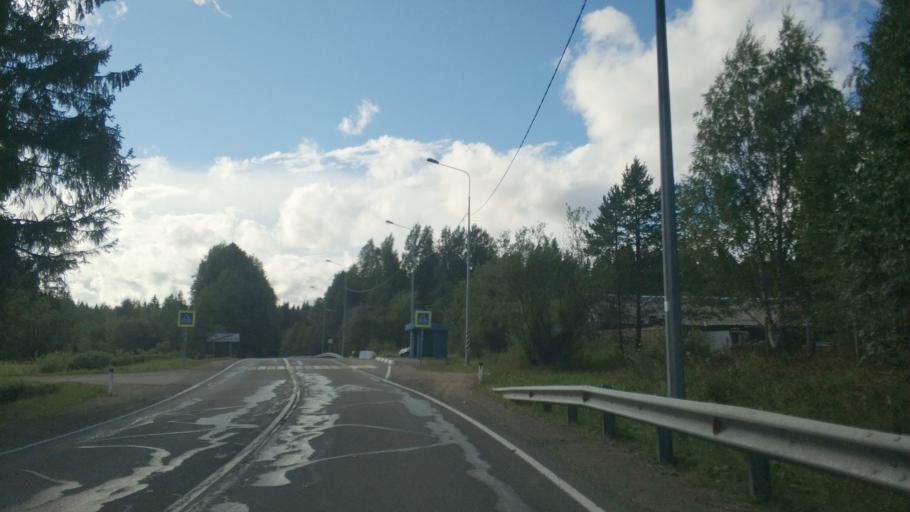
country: RU
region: Republic of Karelia
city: Lakhdenpokh'ya
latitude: 61.5110
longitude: 30.0824
